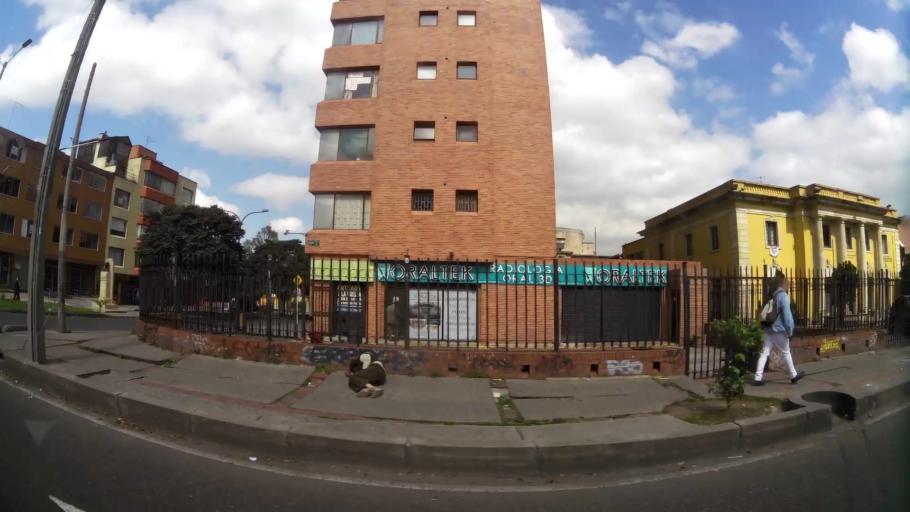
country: CO
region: Bogota D.C.
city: Bogota
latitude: 4.6320
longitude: -74.0679
